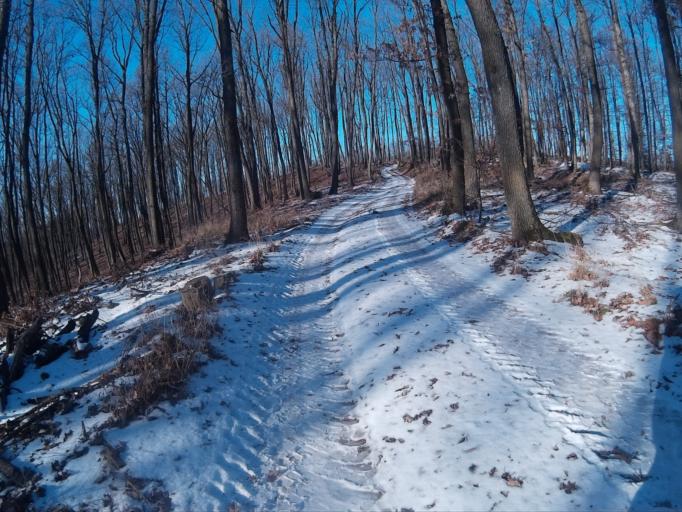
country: HU
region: Borsod-Abauj-Zemplen
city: Putnok
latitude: 48.4103
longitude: 20.4823
